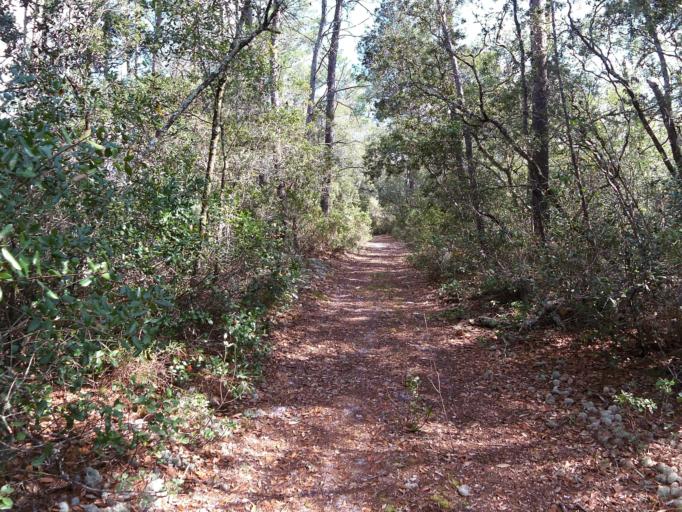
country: US
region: Florida
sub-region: Putnam County
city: Interlachen
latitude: 29.7548
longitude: -81.8177
